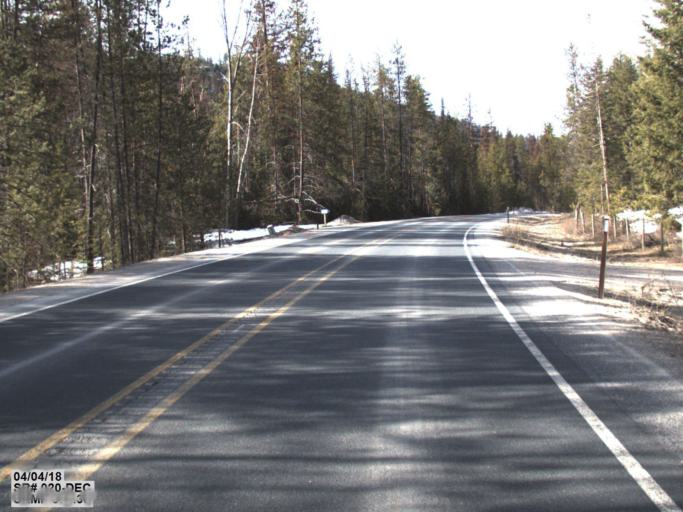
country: US
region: Washington
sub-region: Stevens County
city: Chewelah
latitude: 48.5364
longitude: -117.6063
